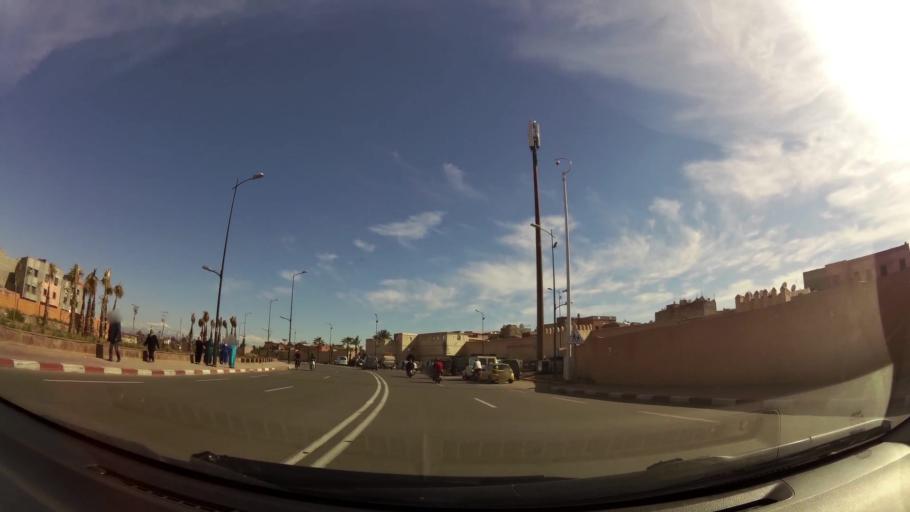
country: MA
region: Marrakech-Tensift-Al Haouz
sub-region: Marrakech
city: Marrakesh
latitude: 31.6351
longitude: -7.9785
